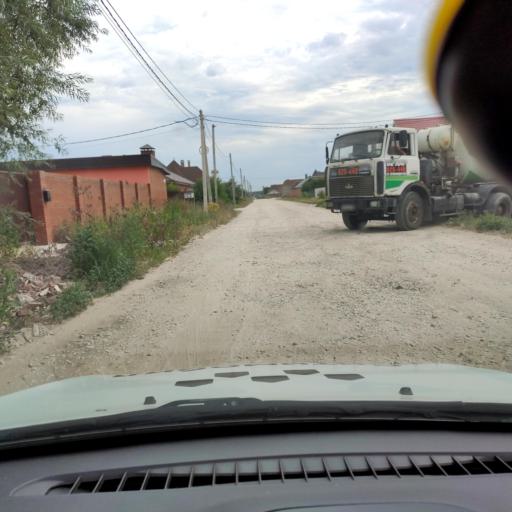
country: RU
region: Samara
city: Podstepki
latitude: 53.5844
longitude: 49.0836
